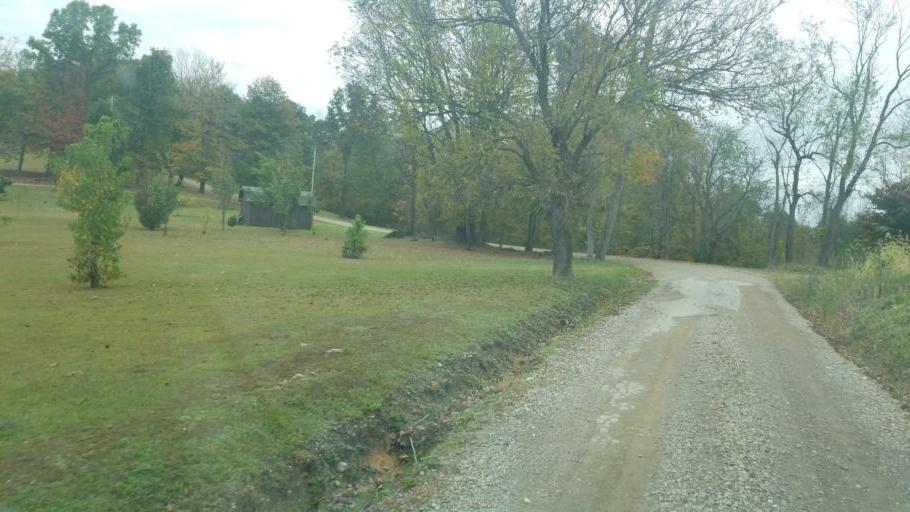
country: US
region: Ohio
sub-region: Wayne County
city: Shreve
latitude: 40.5387
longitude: -82.0842
